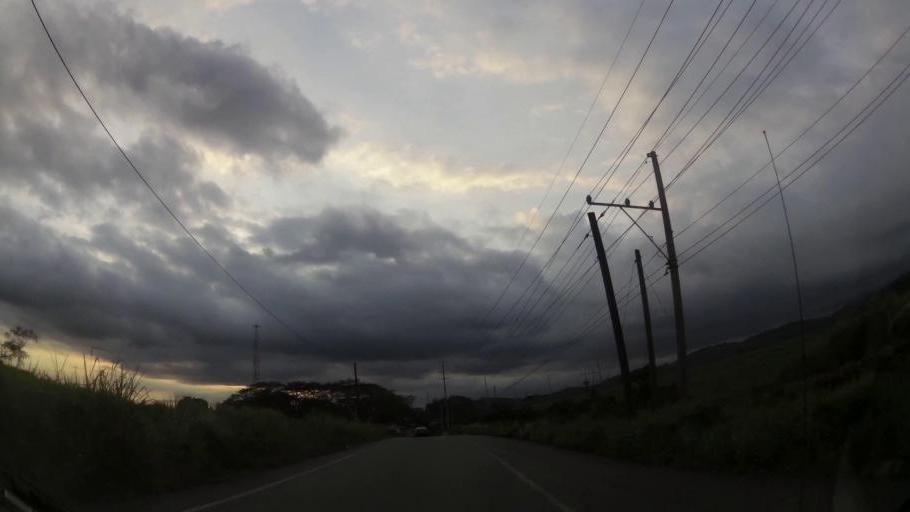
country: GT
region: Suchitepeque
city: Patulul
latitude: 14.3646
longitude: -91.0990
